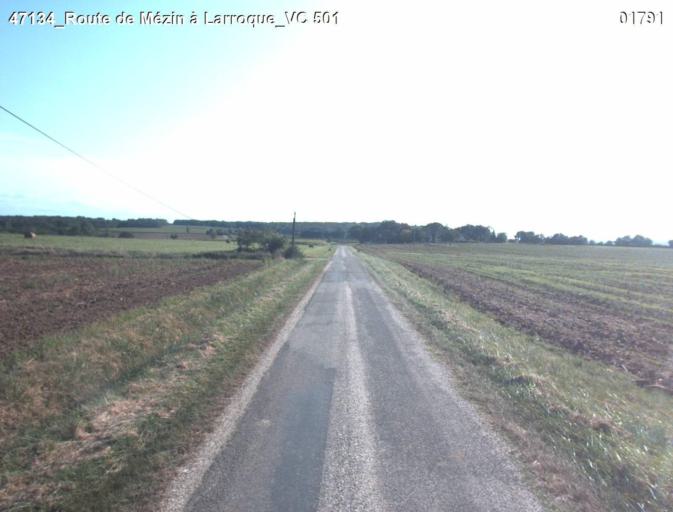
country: FR
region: Aquitaine
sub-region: Departement du Lot-et-Garonne
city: Mezin
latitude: 44.0137
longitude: 0.2777
